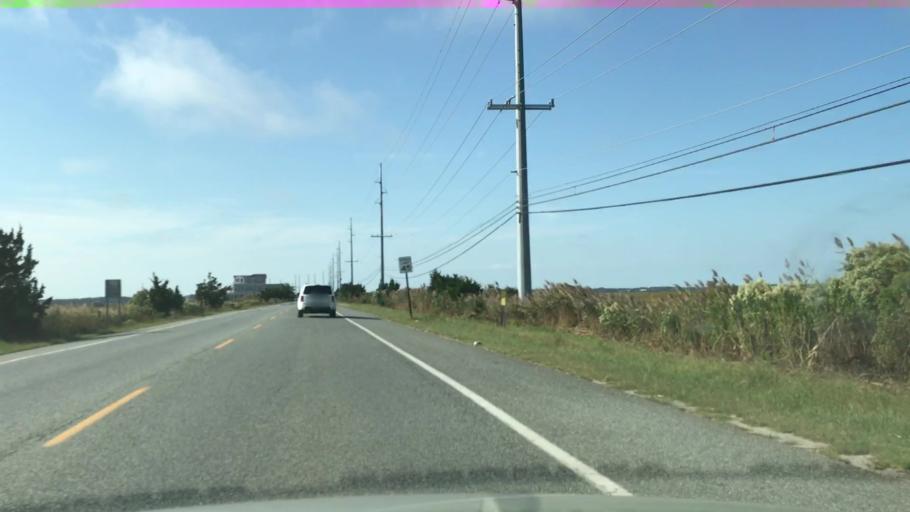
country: US
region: New Jersey
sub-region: Cape May County
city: Cape May Court House
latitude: 39.0627
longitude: -74.7751
